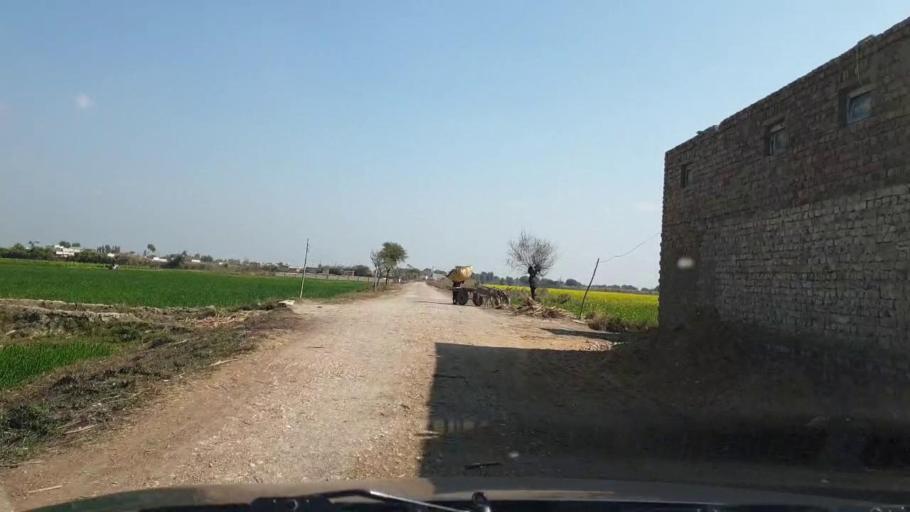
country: PK
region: Sindh
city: Sinjhoro
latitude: 26.0598
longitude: 68.7519
